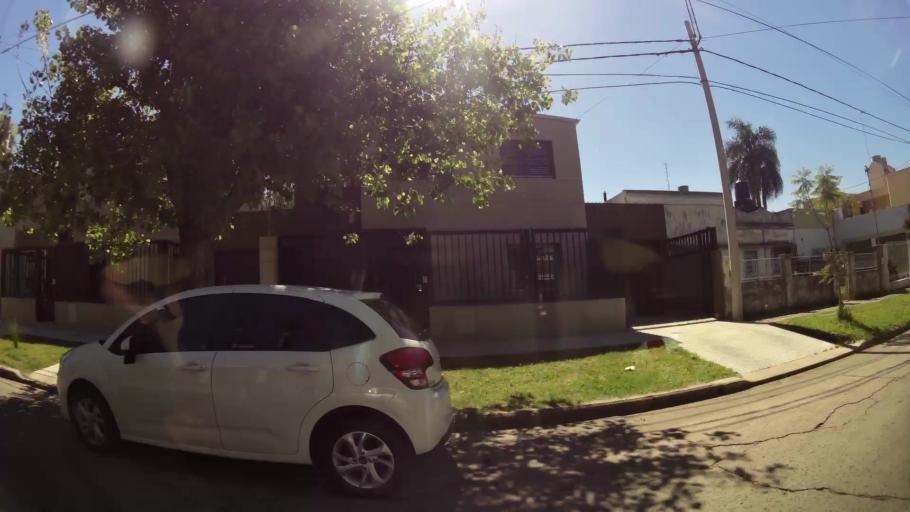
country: AR
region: Santa Fe
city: Santa Fe de la Vera Cruz
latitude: -31.6081
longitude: -60.6712
